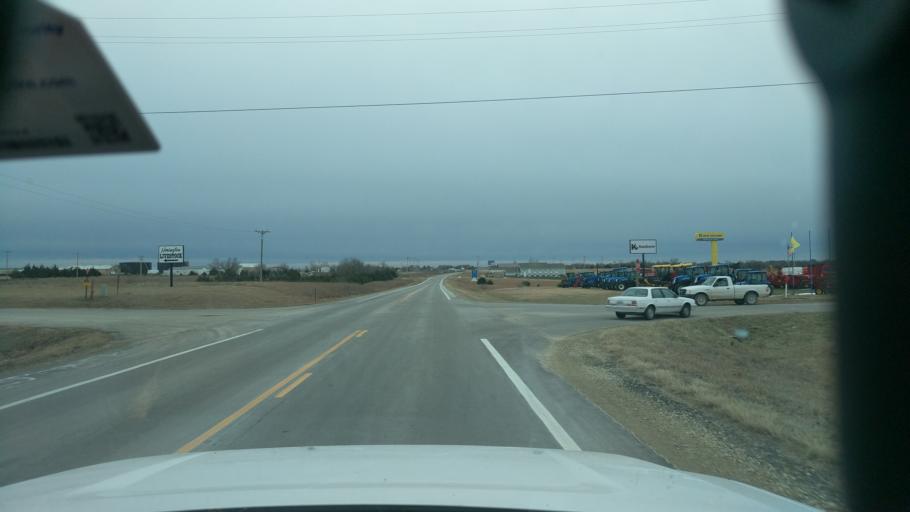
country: US
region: Kansas
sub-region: Dickinson County
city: Herington
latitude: 38.6823
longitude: -96.9304
